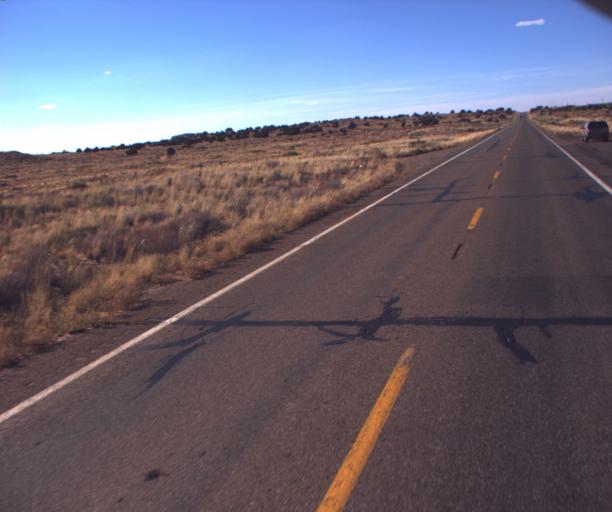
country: US
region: Arizona
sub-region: Coconino County
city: Kaibito
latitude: 36.5881
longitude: -111.1537
